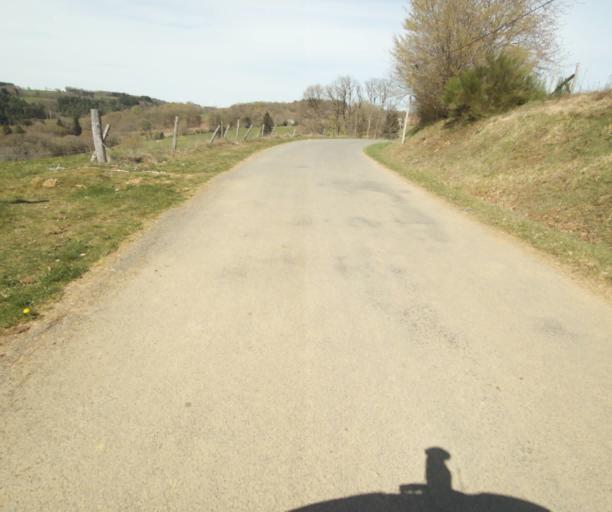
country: FR
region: Limousin
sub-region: Departement de la Correze
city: Seilhac
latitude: 45.3973
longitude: 1.7847
